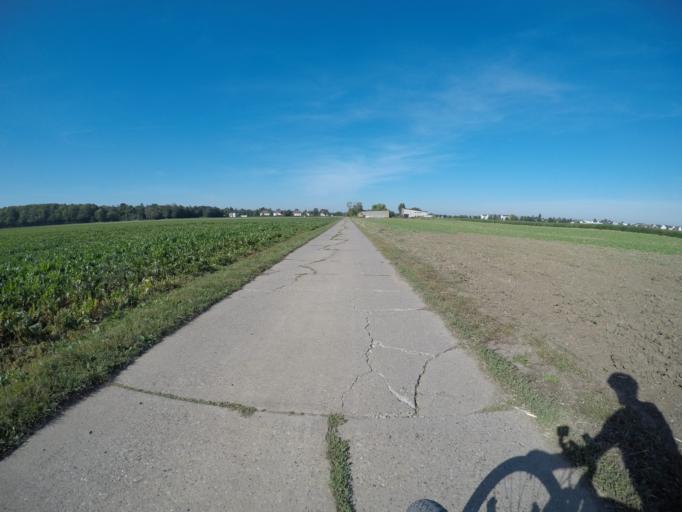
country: DE
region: Hesse
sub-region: Regierungsbezirk Darmstadt
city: Riedstadt
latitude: 49.8245
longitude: 8.5105
